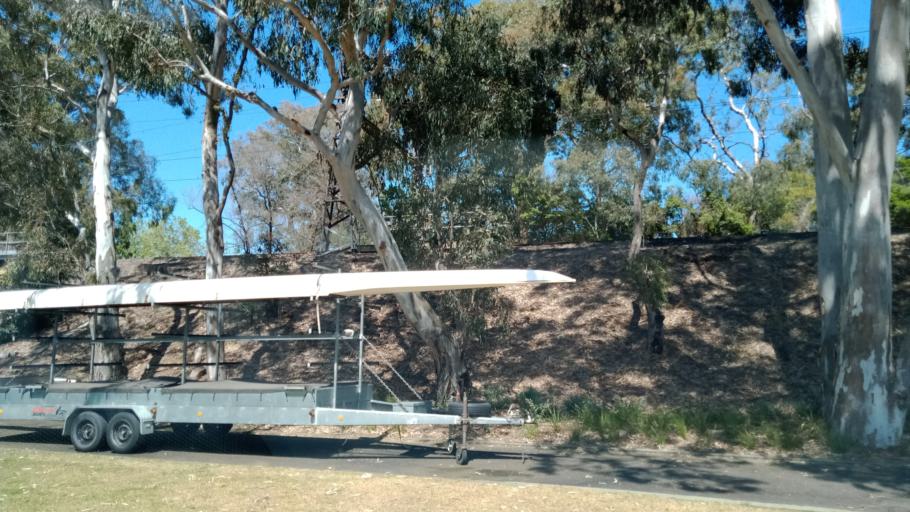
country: AU
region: Victoria
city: Toorak
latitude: -37.8388
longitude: 145.0274
